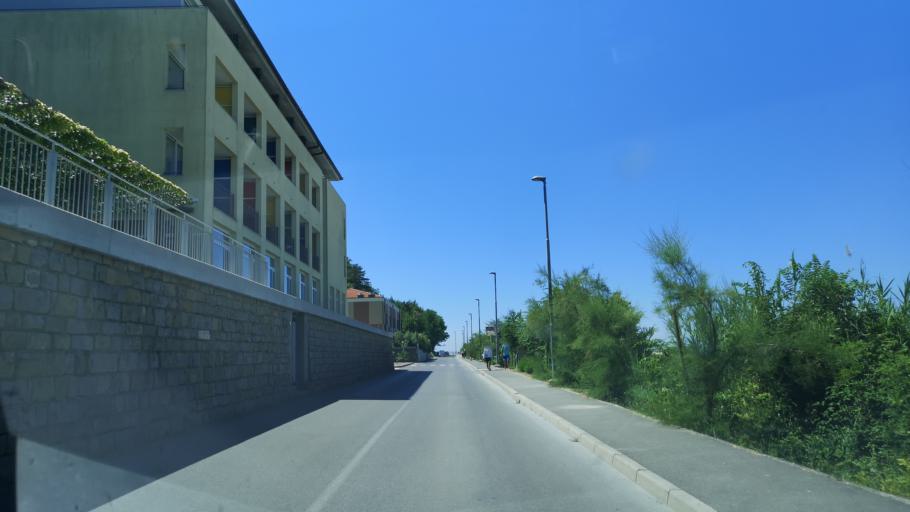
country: SI
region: Piran-Pirano
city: Portoroz
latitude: 45.5254
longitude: 13.6044
